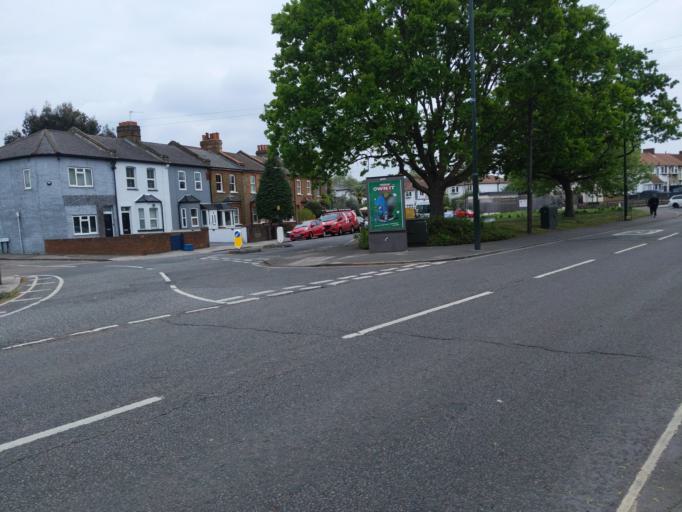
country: GB
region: England
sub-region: Greater London
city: Hounslow
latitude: 51.4537
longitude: -0.3555
